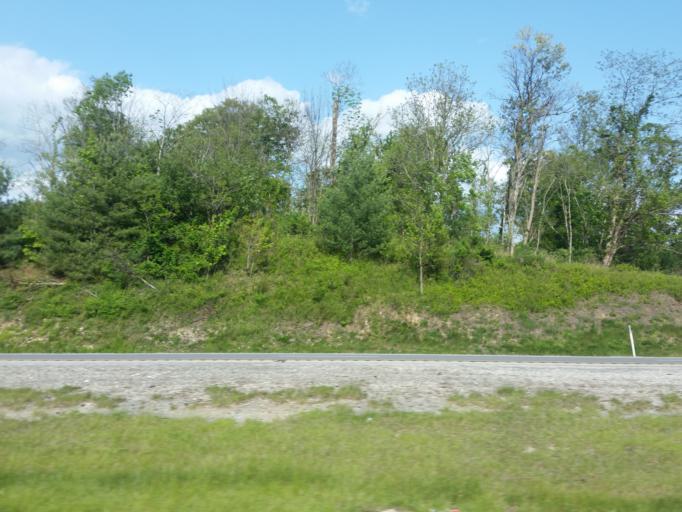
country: US
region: West Virginia
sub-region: Raleigh County
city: Mabscott
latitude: 37.7768
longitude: -81.2211
